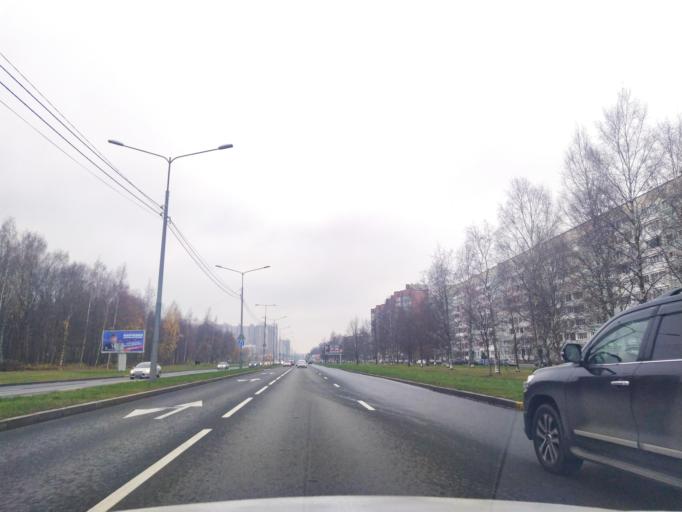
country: RU
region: St.-Petersburg
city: Sosnovka
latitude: 60.0317
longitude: 30.3526
